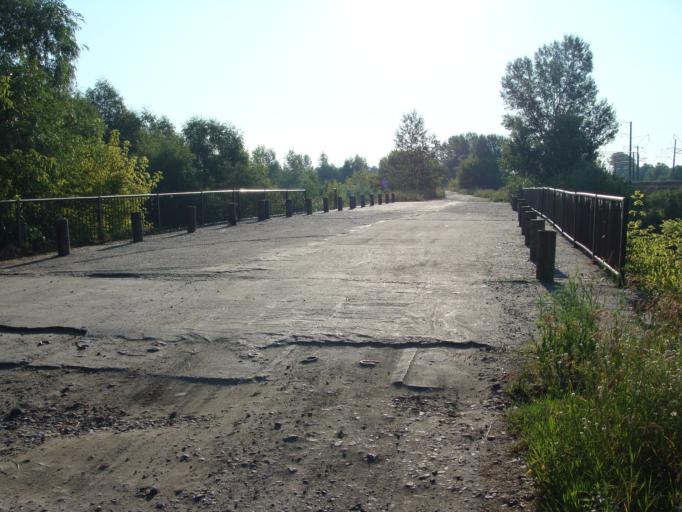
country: RU
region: Altai Krai
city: Novoaltaysk
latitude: 53.3757
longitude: 83.8970
